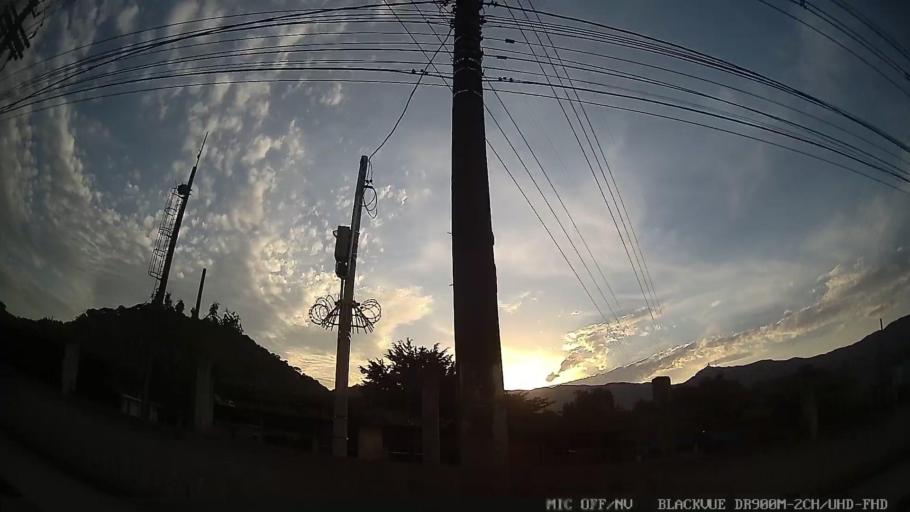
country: BR
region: Sao Paulo
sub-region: Cubatao
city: Cubatao
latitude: -23.8946
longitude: -46.4323
